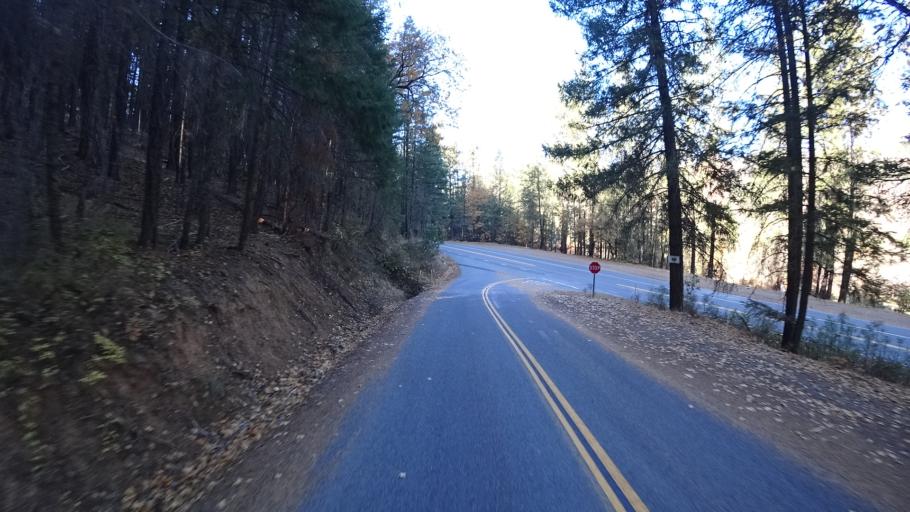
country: US
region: California
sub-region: Siskiyou County
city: Yreka
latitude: 41.8265
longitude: -122.9790
